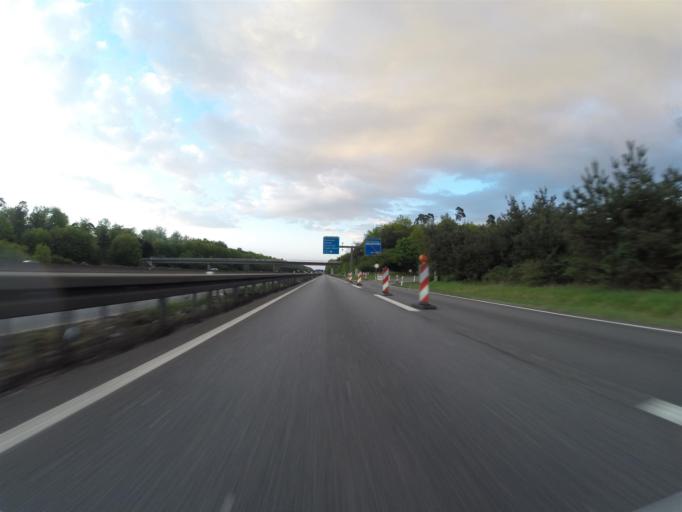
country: DE
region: Hesse
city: Niederrad
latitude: 50.0580
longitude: 8.6072
